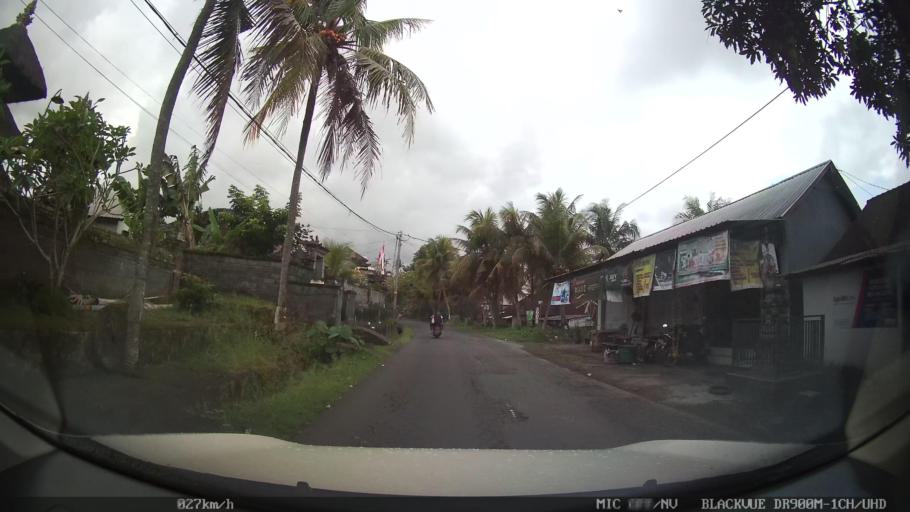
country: ID
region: Bali
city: Banjar Cemenggon
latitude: -8.5535
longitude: 115.1918
